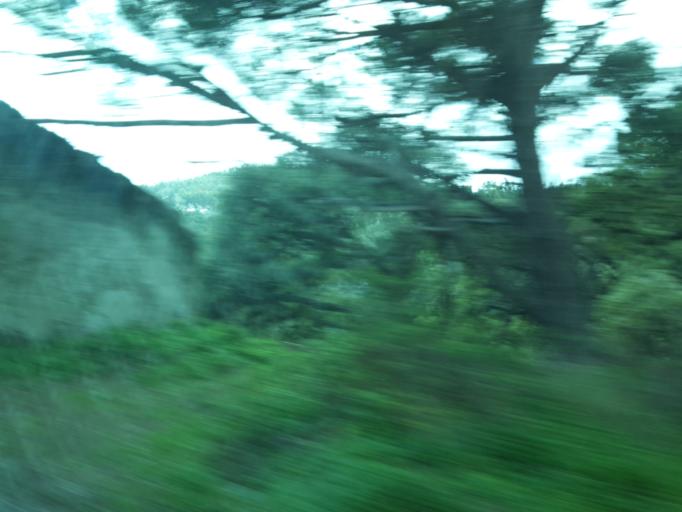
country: PT
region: Faro
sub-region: Monchique
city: Monchique
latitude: 37.2949
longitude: -8.5662
